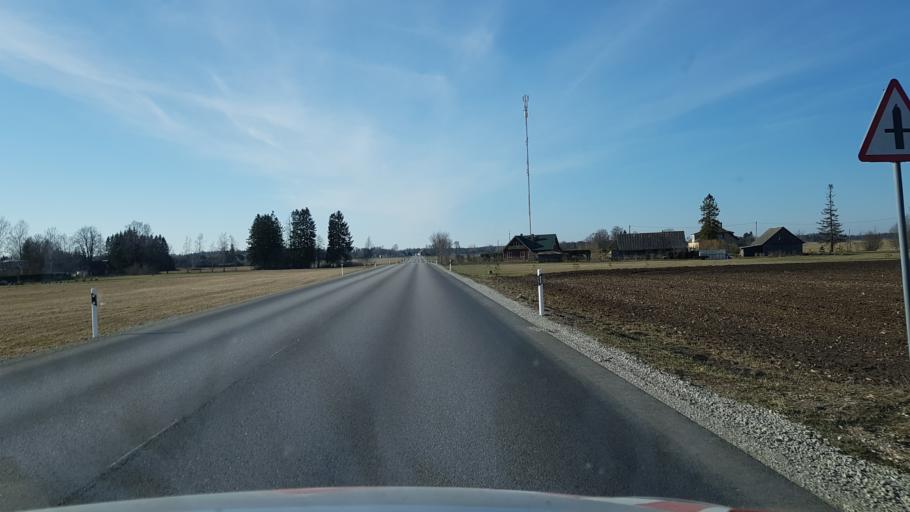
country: EE
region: Laeaene-Virumaa
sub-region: Vinni vald
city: Vinni
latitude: 59.2464
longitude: 26.4783
